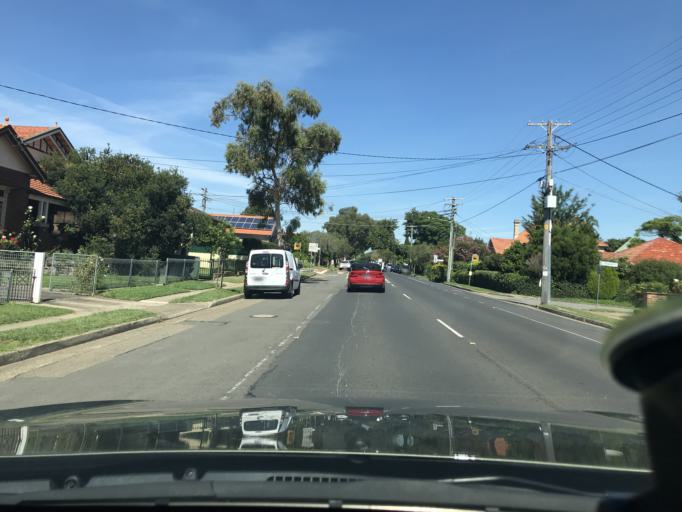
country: AU
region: New South Wales
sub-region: Canada Bay
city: Concord
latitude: -33.8595
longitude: 151.1075
